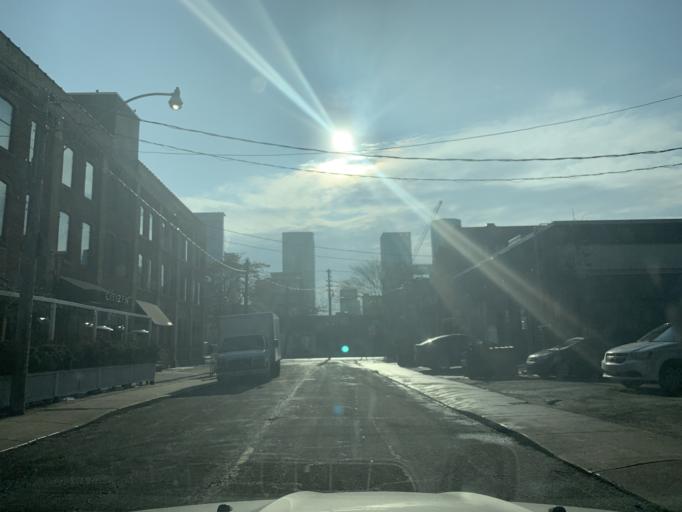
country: CA
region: Ontario
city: Toronto
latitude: 43.6455
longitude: -79.3979
